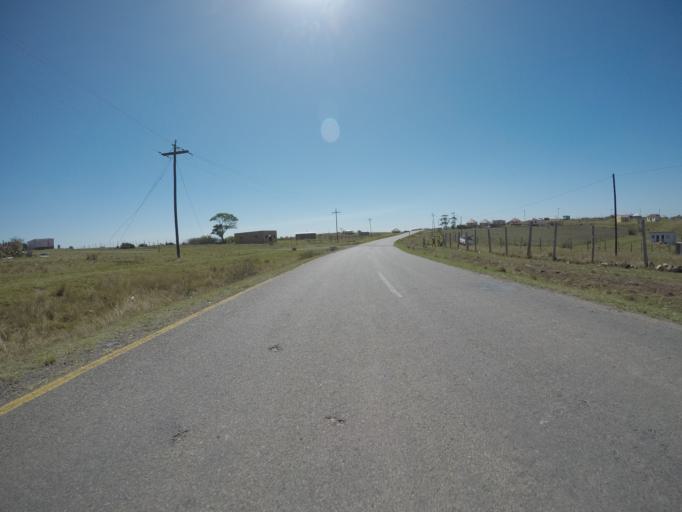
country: ZA
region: Eastern Cape
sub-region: OR Tambo District Municipality
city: Libode
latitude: -31.9084
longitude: 28.9997
